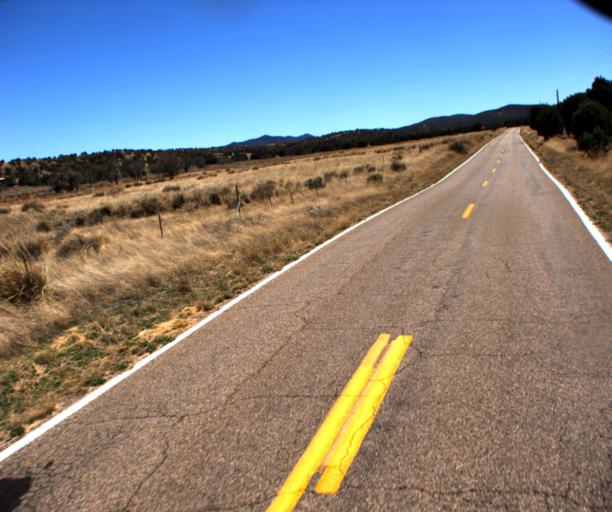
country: US
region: Arizona
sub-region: Cochise County
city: Huachuca City
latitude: 31.5467
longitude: -110.5294
